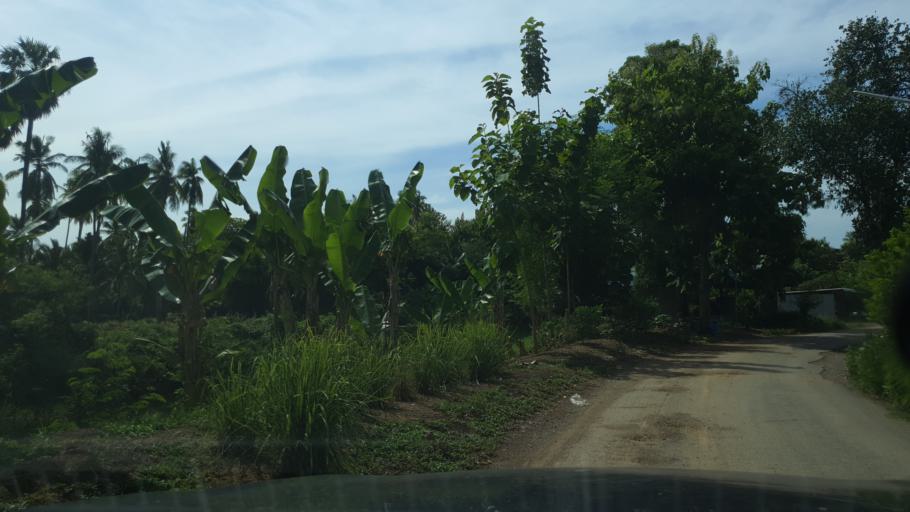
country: TH
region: Sukhothai
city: Sawankhalok
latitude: 17.2168
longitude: 99.7180
